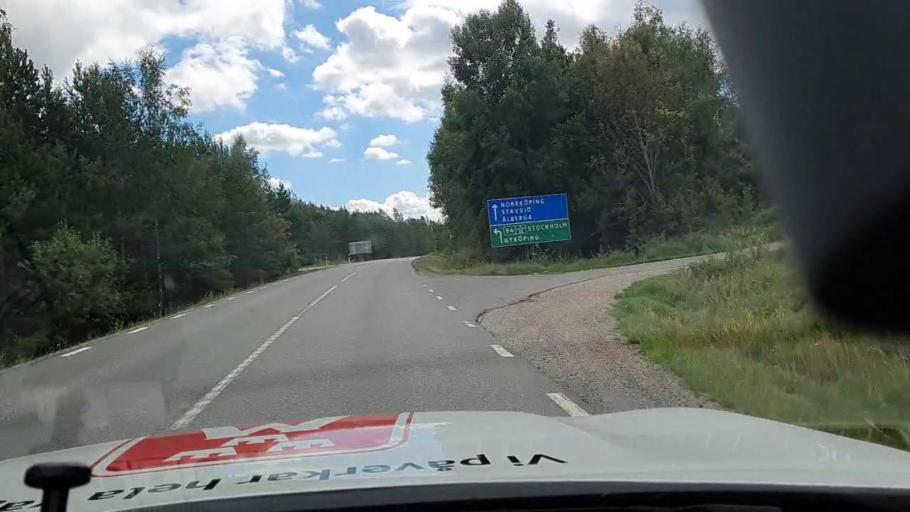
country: SE
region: Soedermanland
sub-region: Nykopings Kommun
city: Olstorp
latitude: 58.7550
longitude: 16.6159
